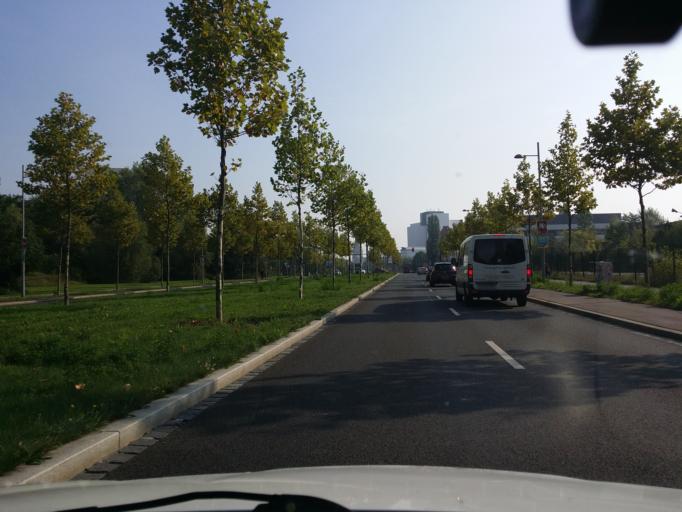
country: DE
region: Saxony
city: Leipzig
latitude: 51.3211
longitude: 12.3875
